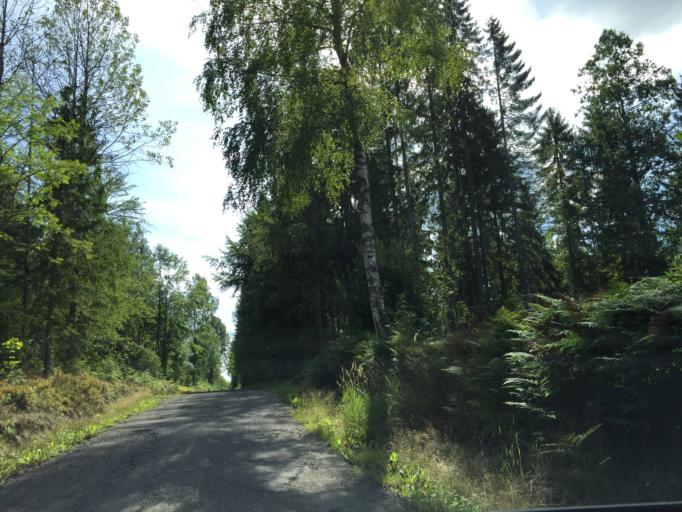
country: NO
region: Vestfold
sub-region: Hof
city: Hof
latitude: 59.4470
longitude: 10.1557
